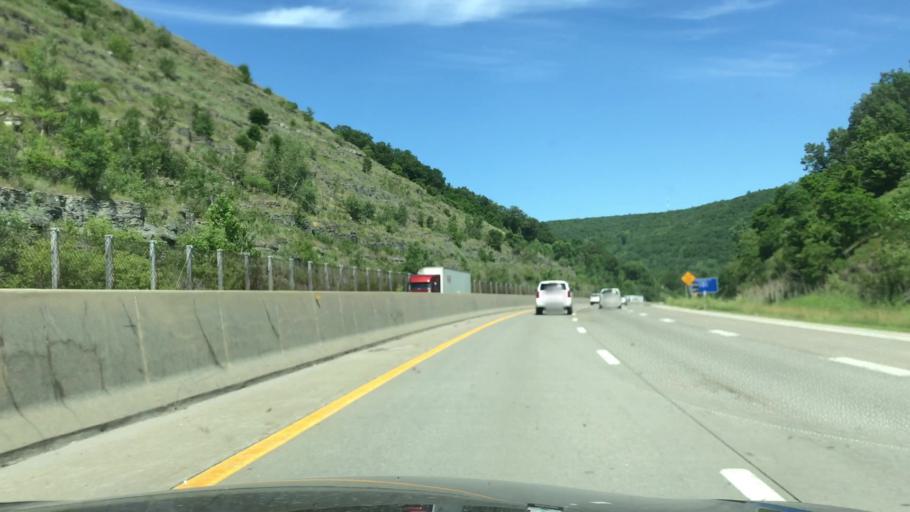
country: US
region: New York
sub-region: Steuben County
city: Corning
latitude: 42.1635
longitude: -77.0654
